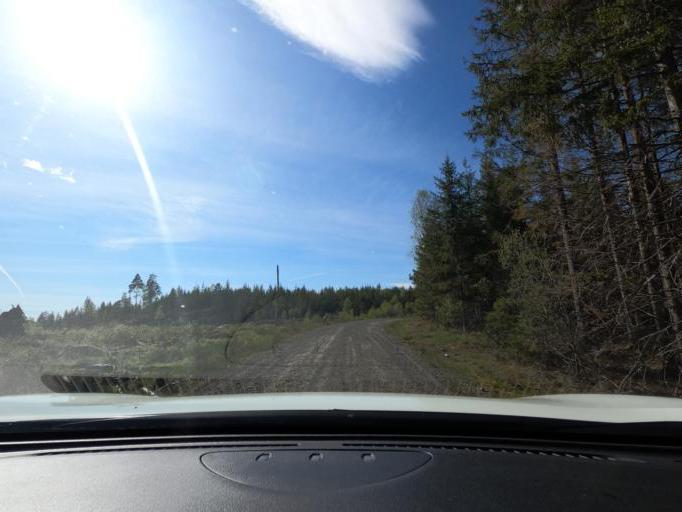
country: SE
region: Vaestra Goetaland
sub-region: Harryda Kommun
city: Ravlanda
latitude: 57.5964
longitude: 12.4746
